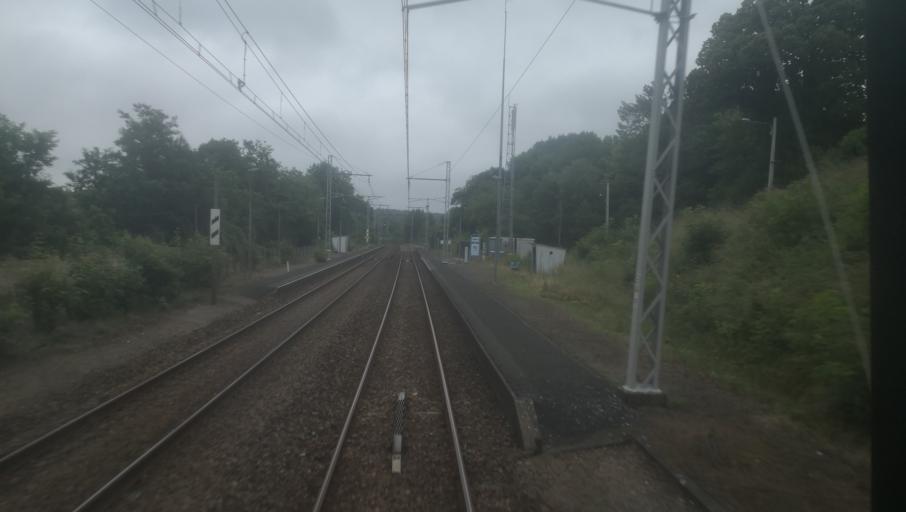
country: FR
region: Centre
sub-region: Departement de l'Indre
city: Saint-Marcel
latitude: 46.6259
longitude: 1.5070
